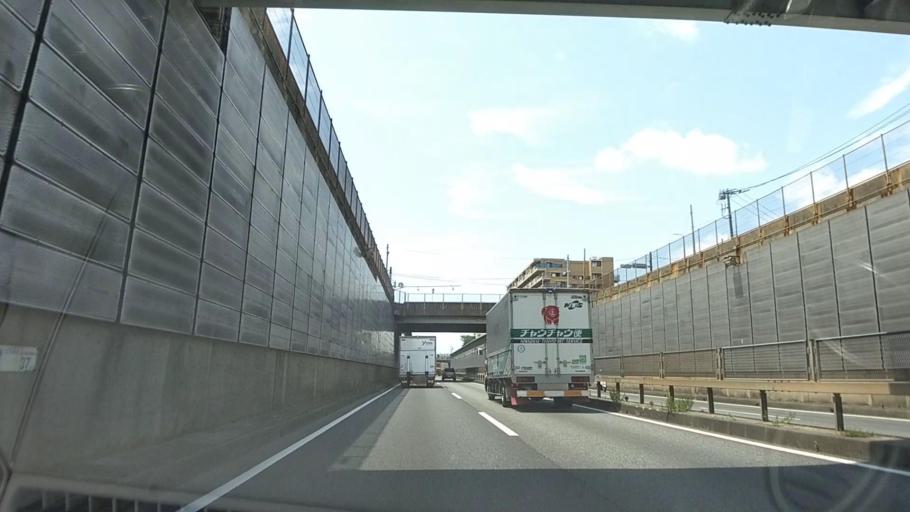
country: JP
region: Kanagawa
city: Minami-rinkan
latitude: 35.4819
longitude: 139.4525
